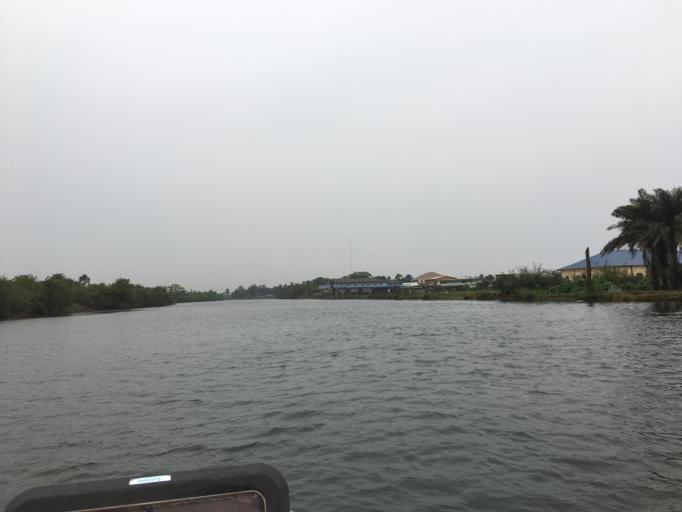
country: LR
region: Montserrado
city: Monrovia
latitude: 6.3849
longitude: -10.7802
